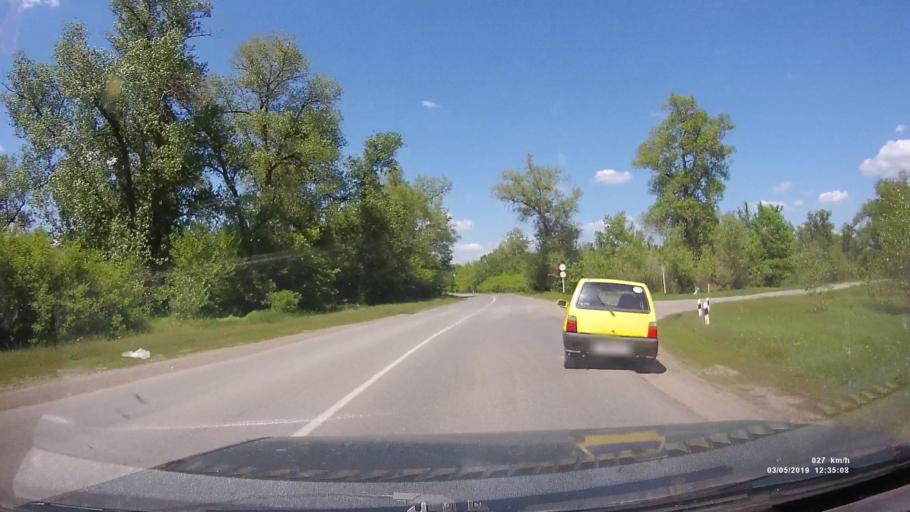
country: RU
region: Rostov
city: Semikarakorsk
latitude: 47.5248
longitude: 40.7625
